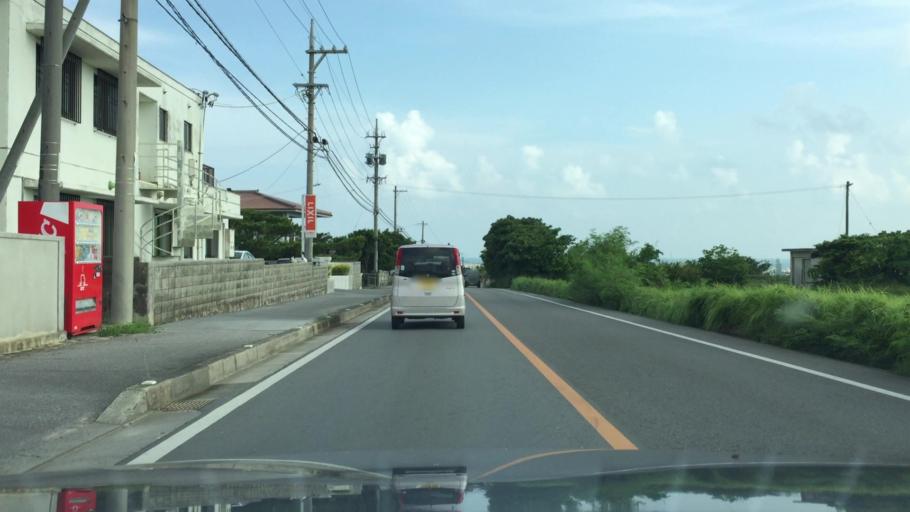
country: JP
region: Okinawa
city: Ishigaki
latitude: 24.3555
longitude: 124.1740
